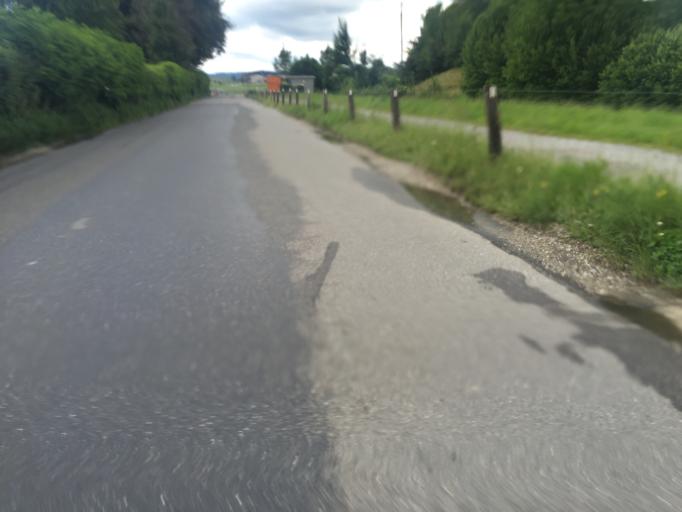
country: CH
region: Bern
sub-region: Bern-Mittelland District
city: Frauenkappelen
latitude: 46.9330
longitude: 7.3730
